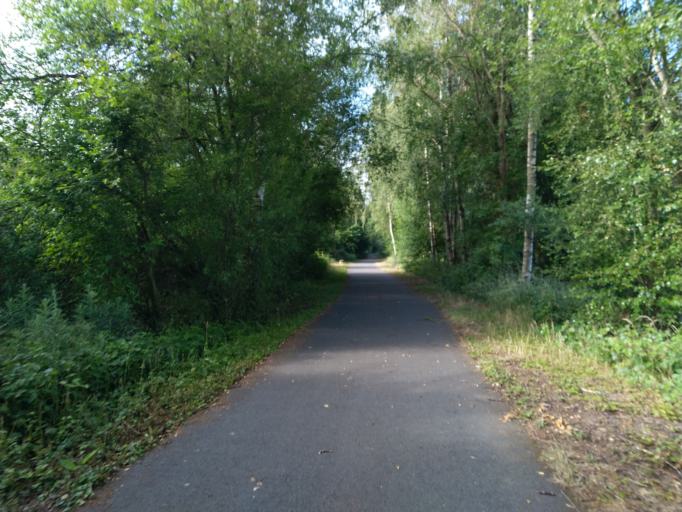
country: BE
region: Wallonia
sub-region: Province du Hainaut
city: Erquelinnes
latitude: 50.3368
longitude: 4.1003
